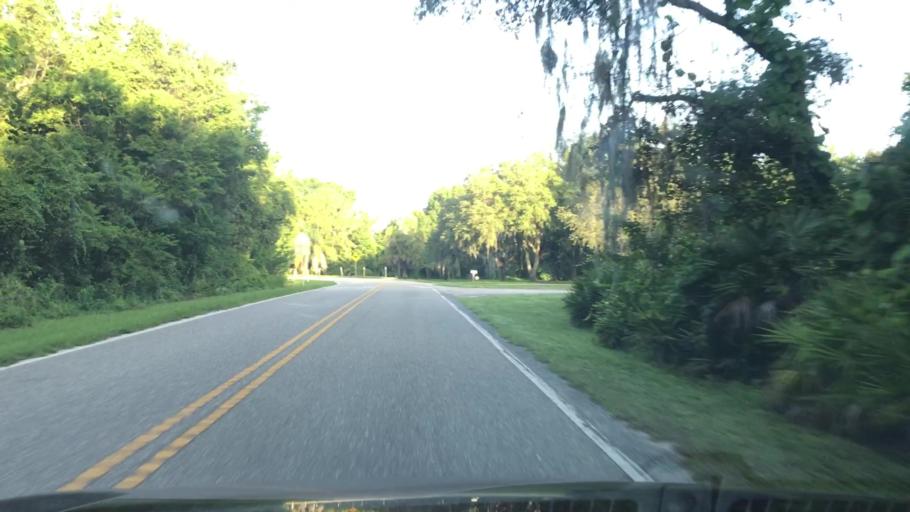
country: US
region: Florida
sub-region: Sarasota County
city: Fruitville
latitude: 27.3274
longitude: -82.4214
